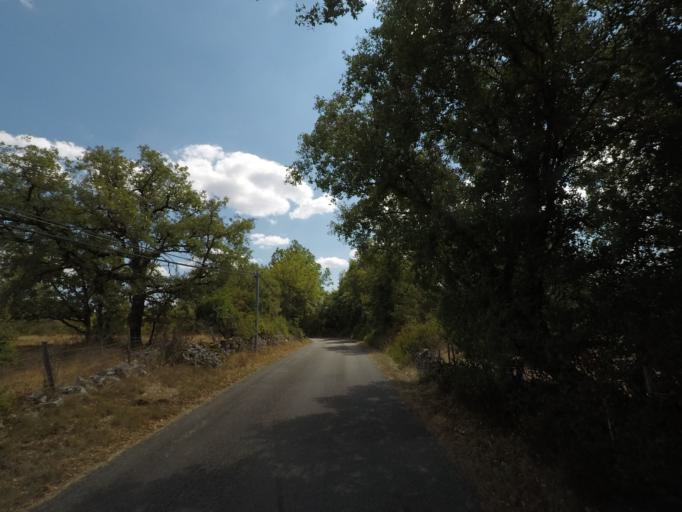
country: FR
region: Midi-Pyrenees
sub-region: Departement du Lot
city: Cajarc
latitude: 44.5651
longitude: 1.6712
